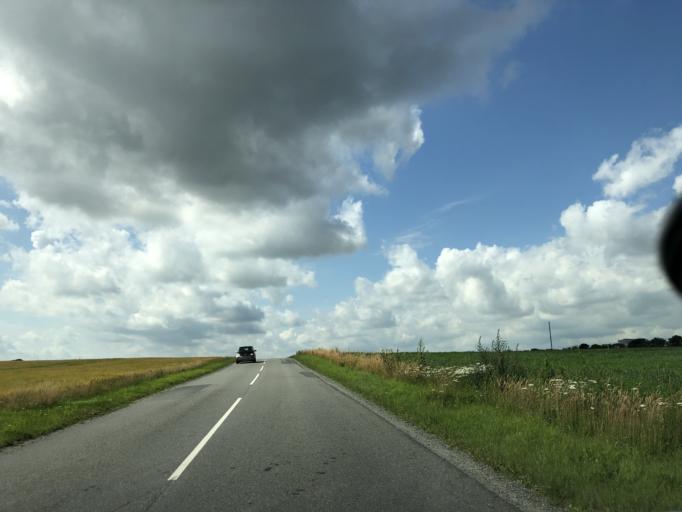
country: DK
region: Central Jutland
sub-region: Ikast-Brande Kommune
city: Brande
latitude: 55.9587
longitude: 9.1471
